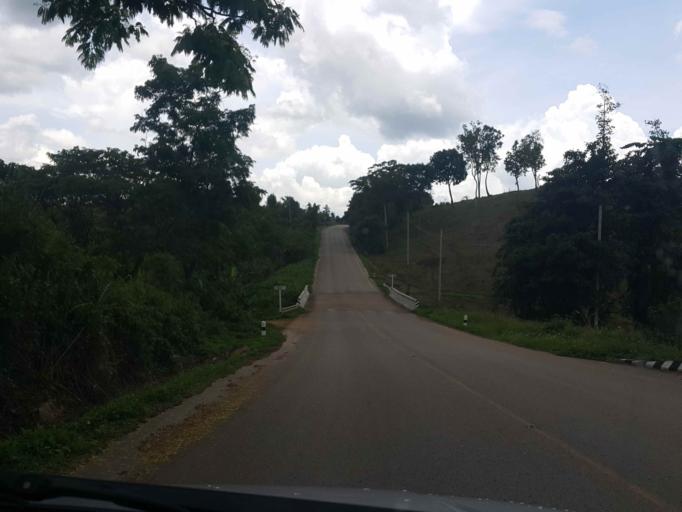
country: TH
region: Lampang
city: Ngao
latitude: 18.9414
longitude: 100.0767
